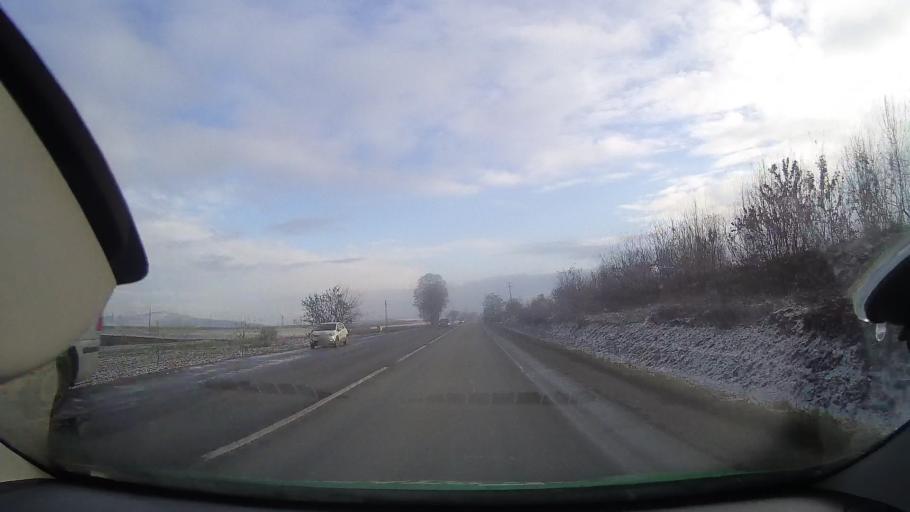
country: RO
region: Mures
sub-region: Comuna Cuci
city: Cuci
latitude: 46.4598
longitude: 24.1671
